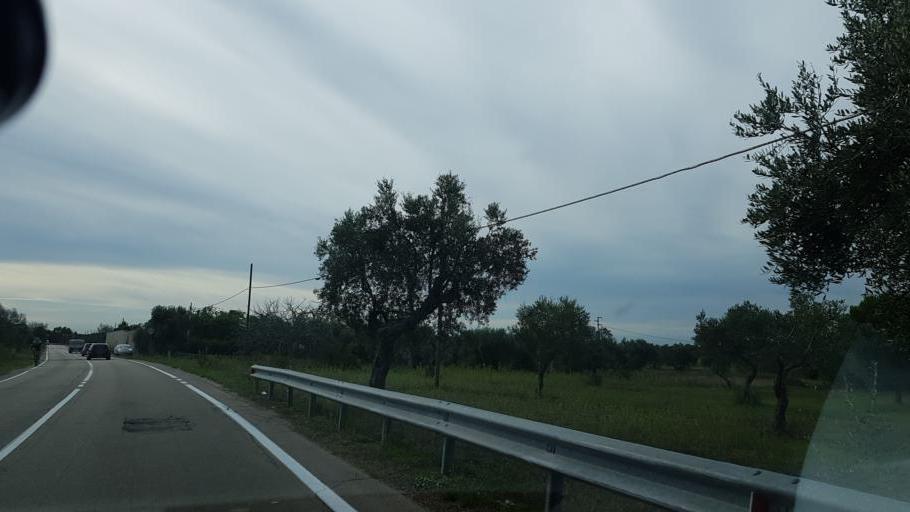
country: IT
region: Apulia
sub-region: Provincia di Lecce
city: Struda
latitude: 40.3565
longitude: 18.3164
